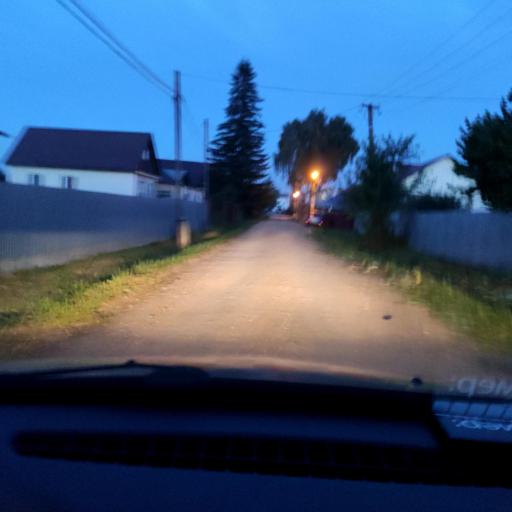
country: RU
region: Bashkortostan
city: Iglino
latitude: 54.8356
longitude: 56.4107
